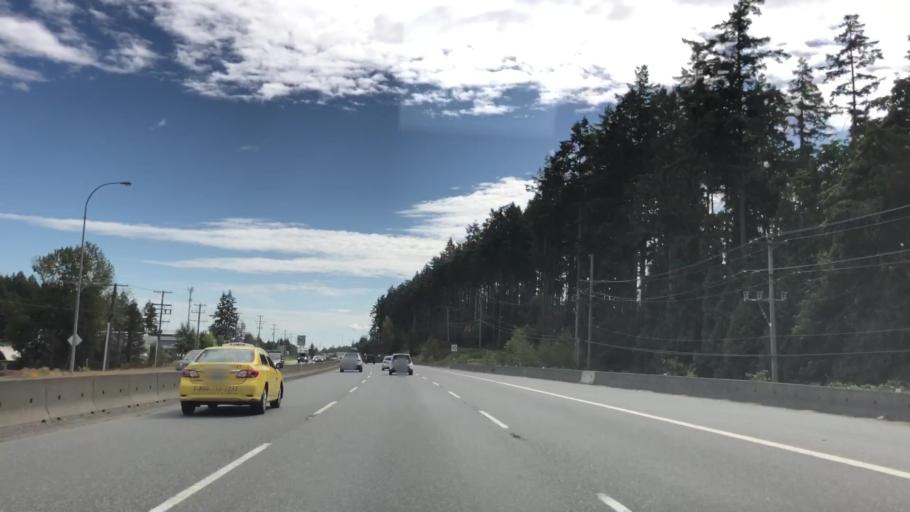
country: CA
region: British Columbia
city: Nanaimo
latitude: 49.1090
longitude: -123.9005
